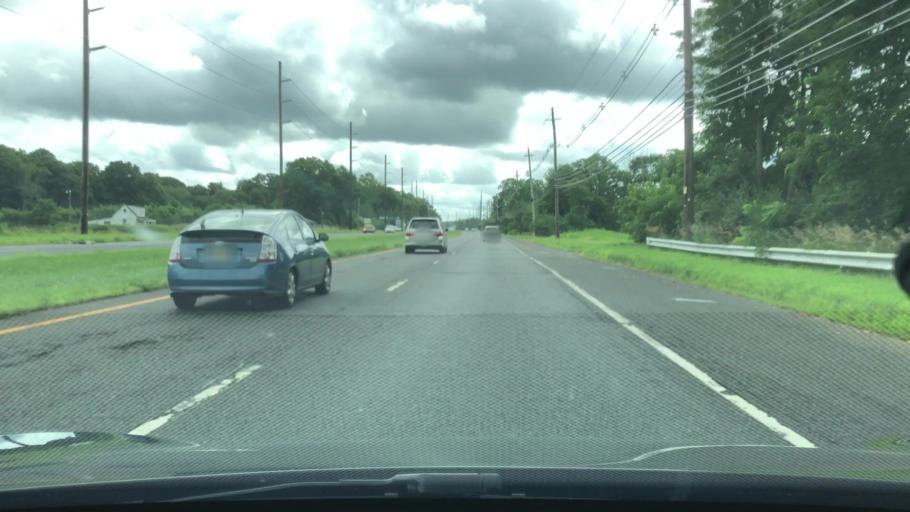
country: US
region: New Jersey
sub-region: Mercer County
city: Twin Rivers
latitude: 40.2636
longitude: -74.4499
